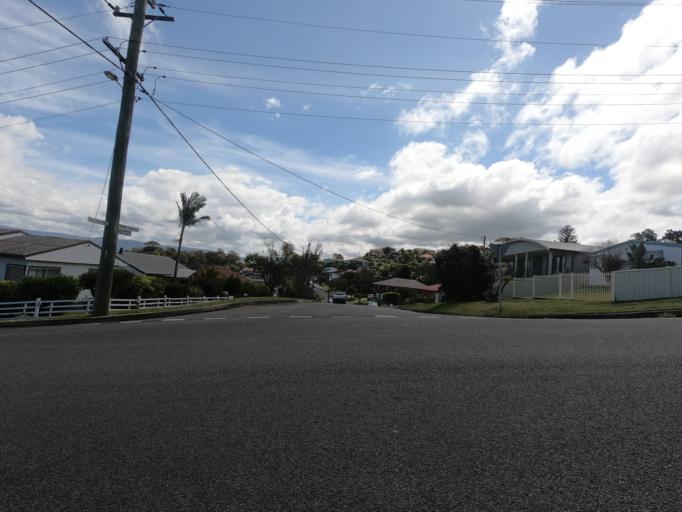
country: AU
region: New South Wales
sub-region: Wollongong
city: Lake Heights
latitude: -34.4876
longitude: 150.8657
